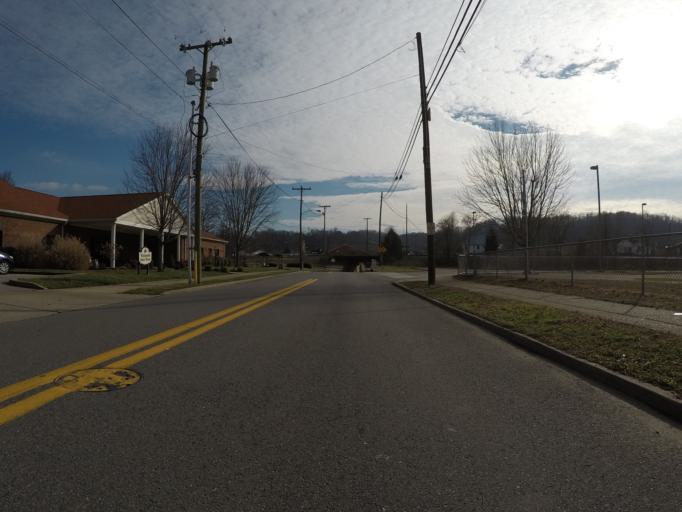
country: US
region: West Virginia
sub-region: Cabell County
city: Barboursville
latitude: 38.4073
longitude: -82.2952
